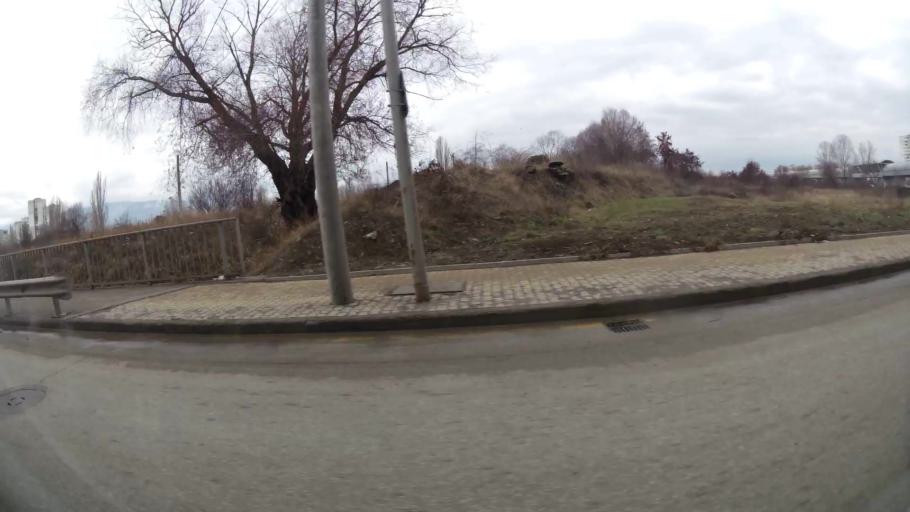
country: BG
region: Sofia-Capital
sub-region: Stolichna Obshtina
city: Sofia
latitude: 42.7416
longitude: 23.2858
